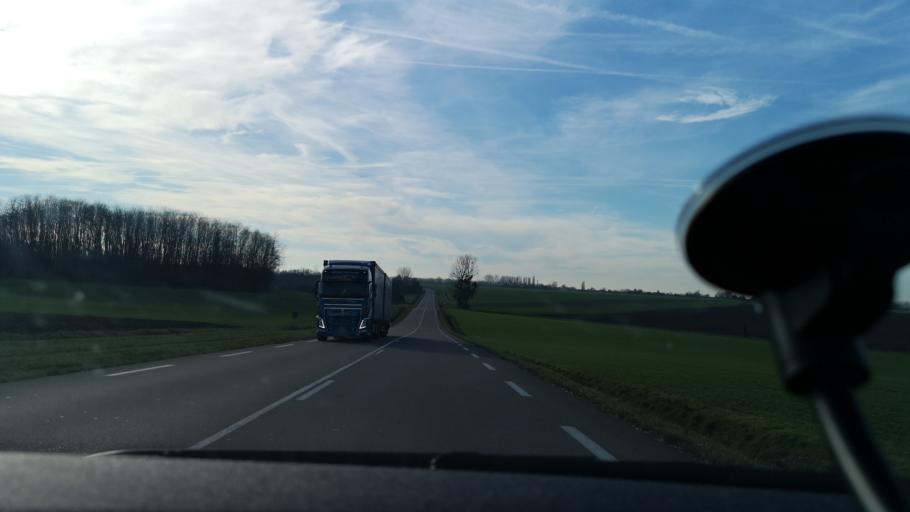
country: FR
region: Bourgogne
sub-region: Departement de la Cote-d'Or
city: Seurre
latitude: 46.9288
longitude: 5.1313
